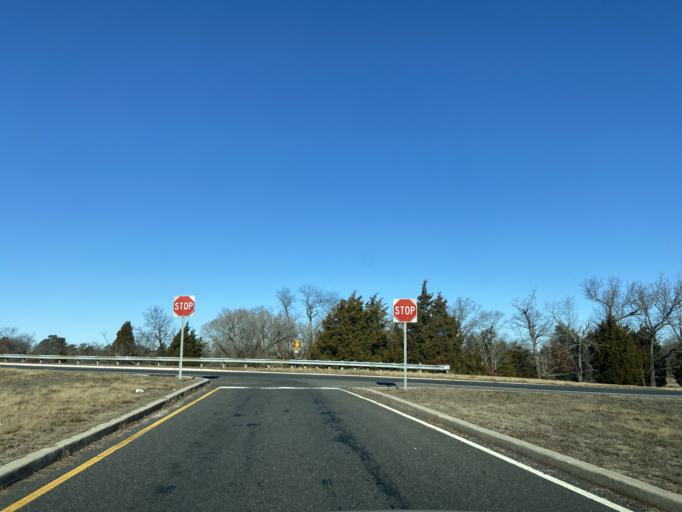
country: US
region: New Jersey
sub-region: Gloucester County
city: Newfield
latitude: 39.5216
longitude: -75.0674
